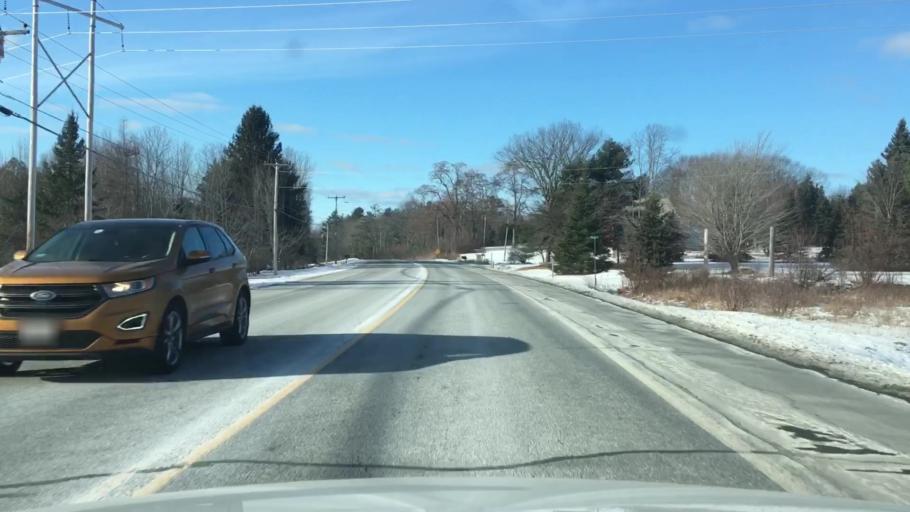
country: US
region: Maine
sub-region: Penobscot County
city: Holden
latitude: 44.8011
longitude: -68.5978
